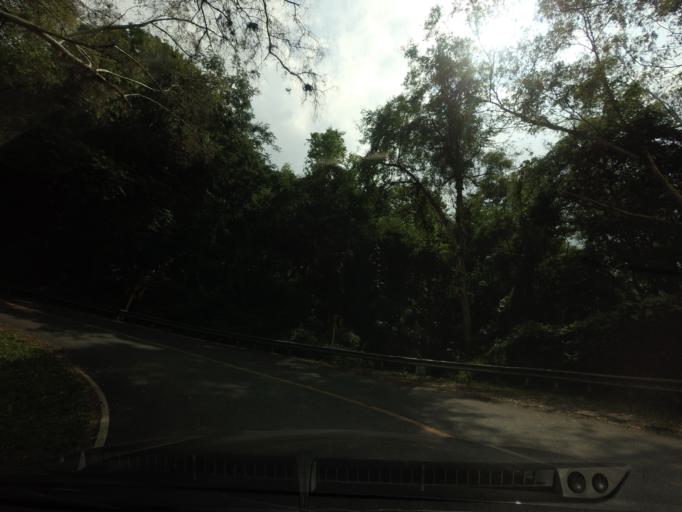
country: TH
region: Nan
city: Pua
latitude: 19.1837
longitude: 101.0027
